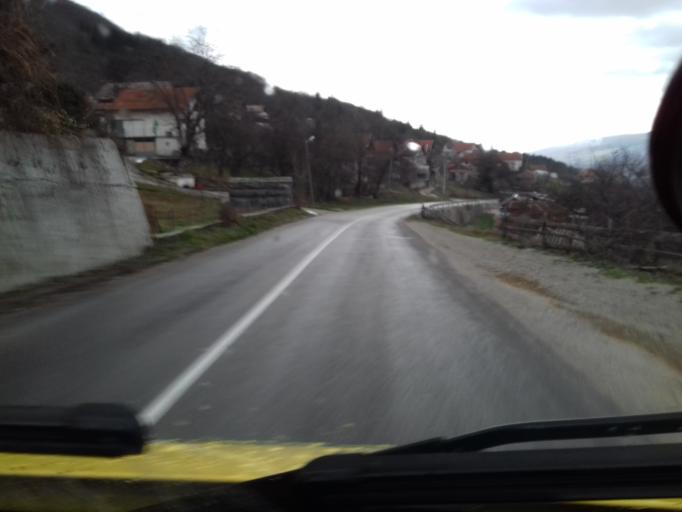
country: BA
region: Federation of Bosnia and Herzegovina
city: Turbe
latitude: 44.2696
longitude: 17.5223
